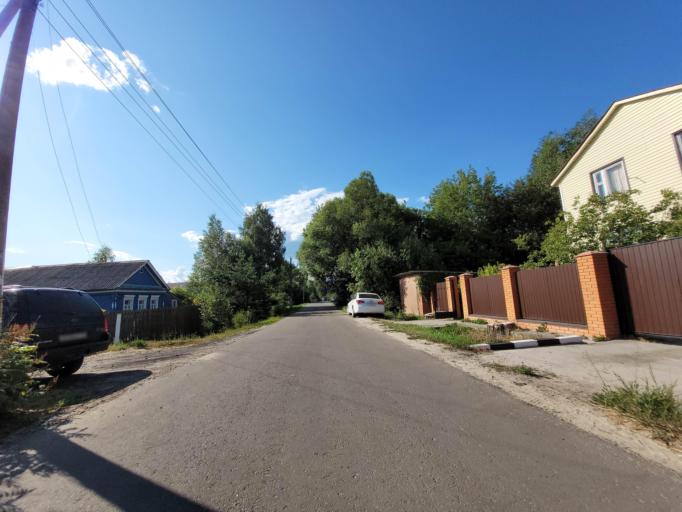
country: RU
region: Moskovskaya
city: Konobeyevo
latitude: 55.4104
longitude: 38.6983
